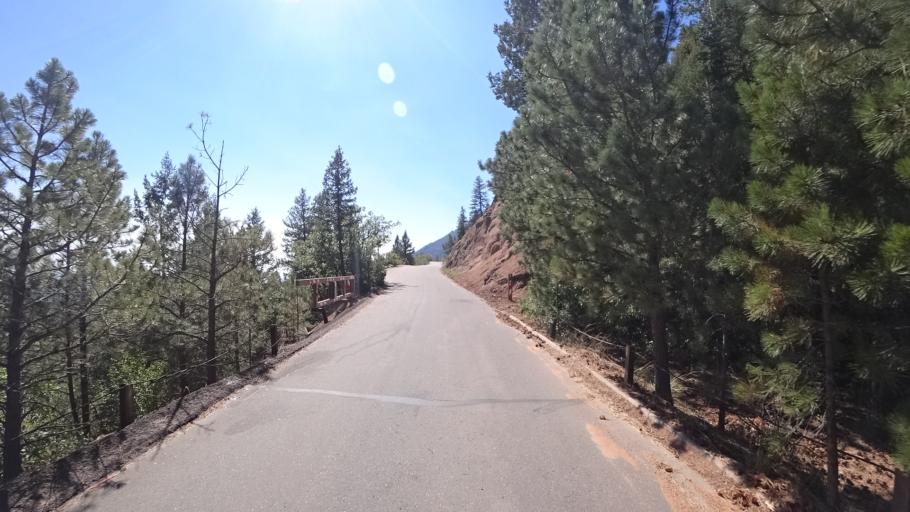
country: US
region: Colorado
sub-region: El Paso County
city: Colorado Springs
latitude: 38.8026
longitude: -104.8774
